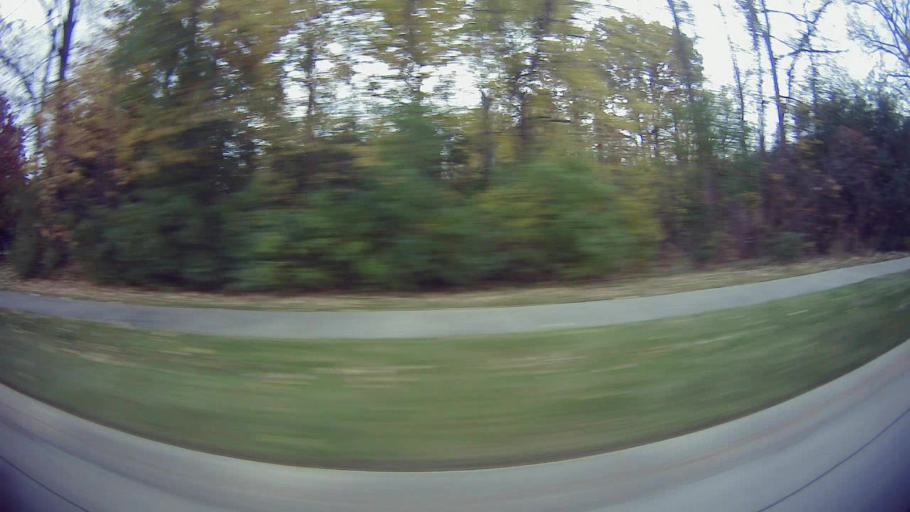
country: US
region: Michigan
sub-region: Oakland County
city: Farmington Hills
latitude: 42.4917
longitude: -83.3581
